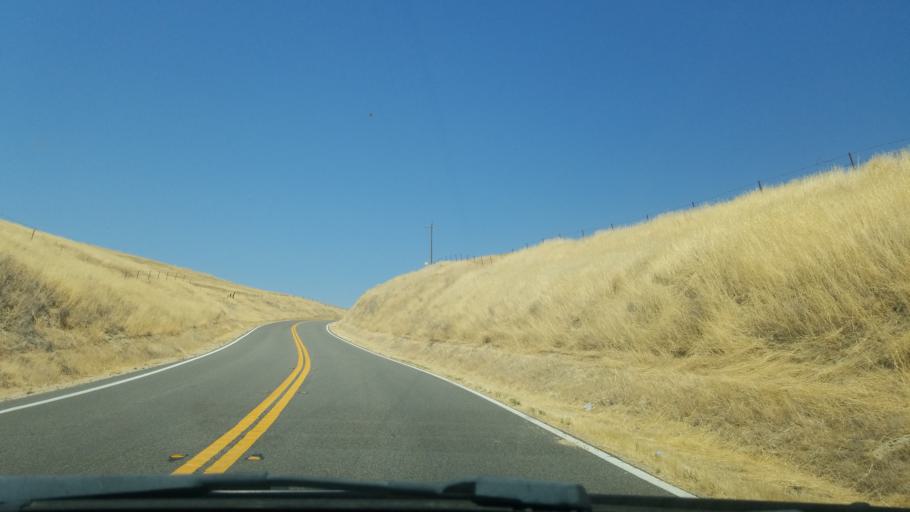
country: US
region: California
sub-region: San Luis Obispo County
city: Shandon
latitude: 35.5904
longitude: -120.4214
